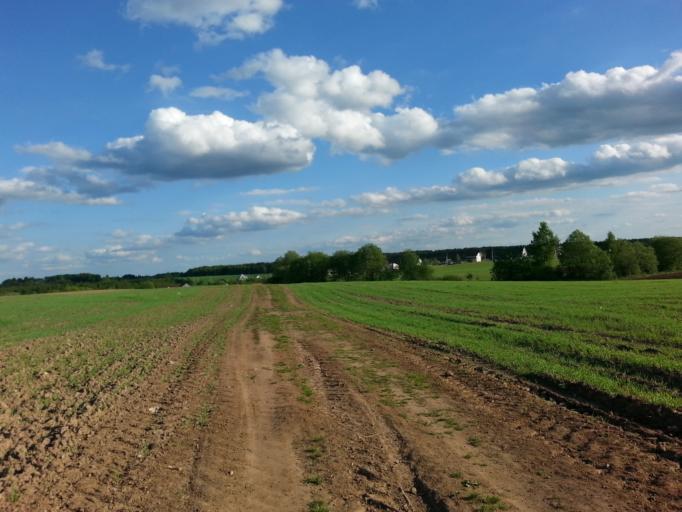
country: BY
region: Minsk
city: Narach
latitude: 54.9404
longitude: 26.7019
